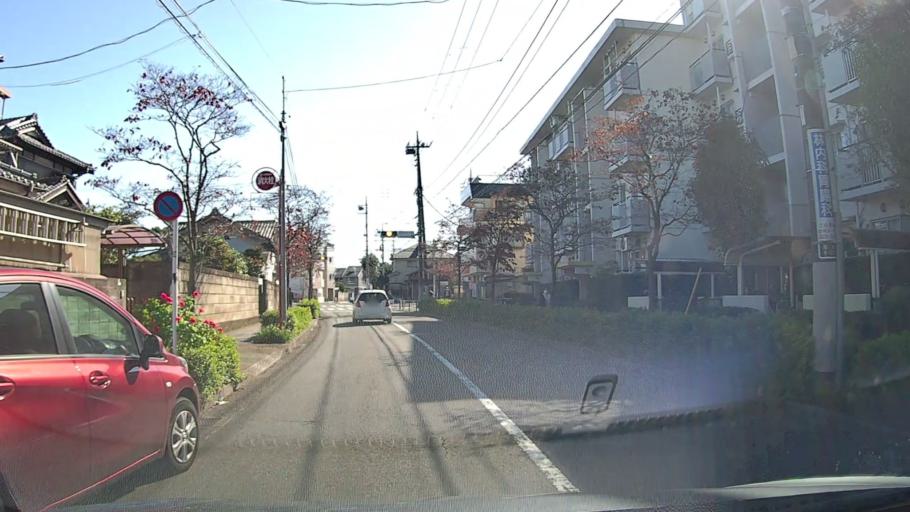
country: JP
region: Saitama
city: Wako
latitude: 35.7516
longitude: 139.6254
